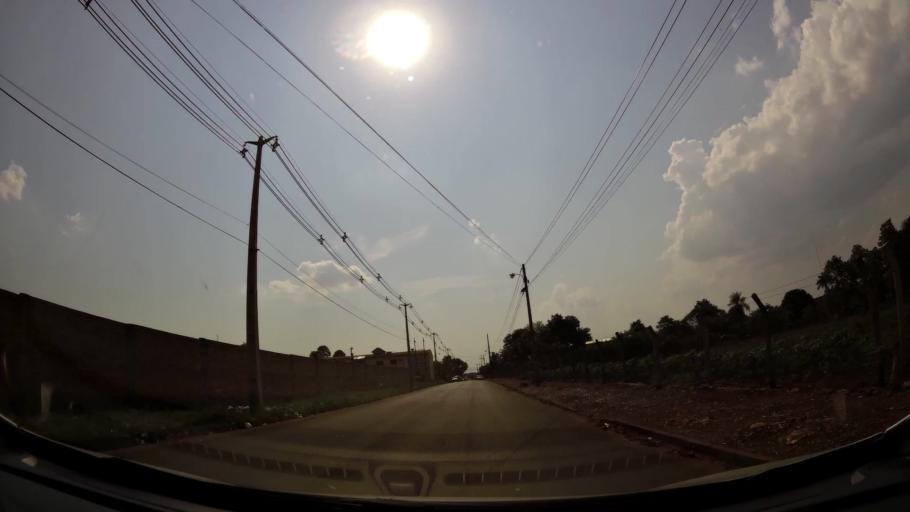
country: PY
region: Alto Parana
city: Ciudad del Este
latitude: -25.5031
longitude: -54.6325
